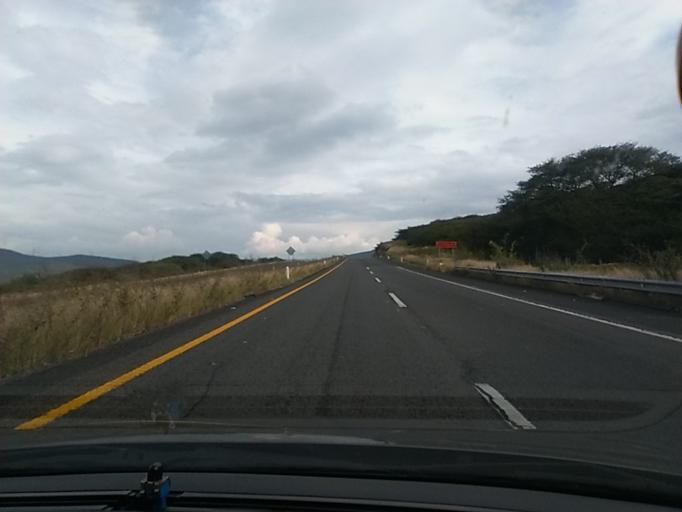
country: MX
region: Michoacan
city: Ixtlan
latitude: 20.2356
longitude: -102.3828
